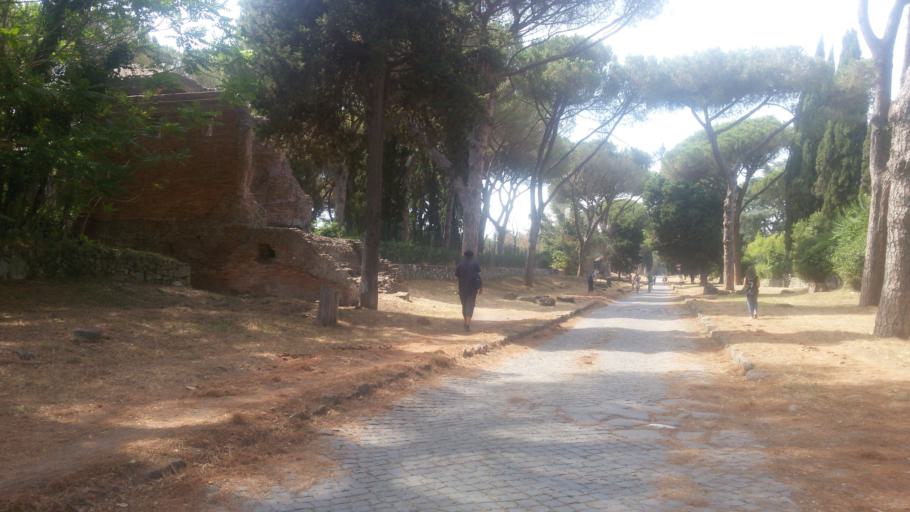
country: IT
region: Latium
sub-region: Citta metropolitana di Roma Capitale
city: Rome
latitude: 41.8361
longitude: 12.5385
